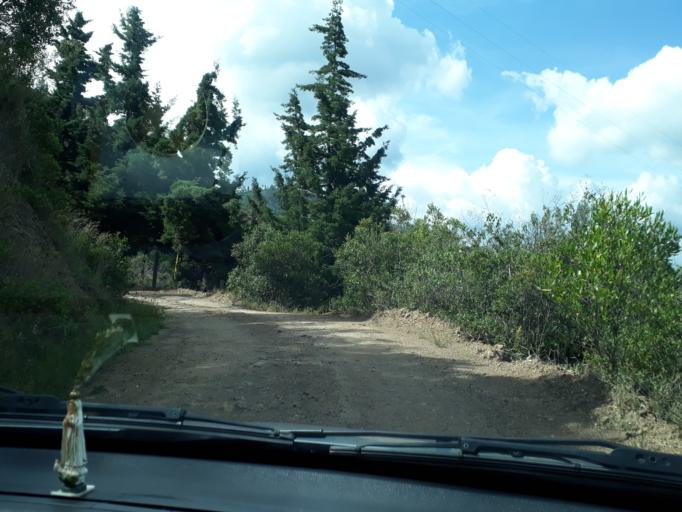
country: CO
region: Boyaca
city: Santa Rosa de Viterbo
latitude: 5.8571
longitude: -72.9703
